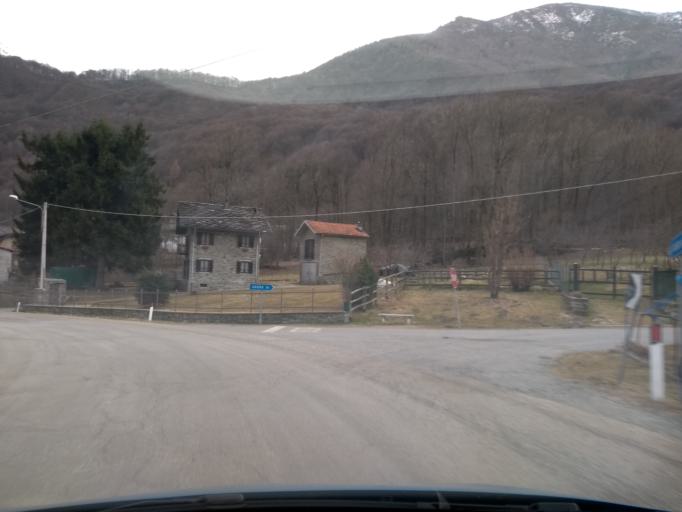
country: IT
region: Piedmont
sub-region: Provincia di Torino
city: Lemie
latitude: 45.2250
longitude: 7.3057
